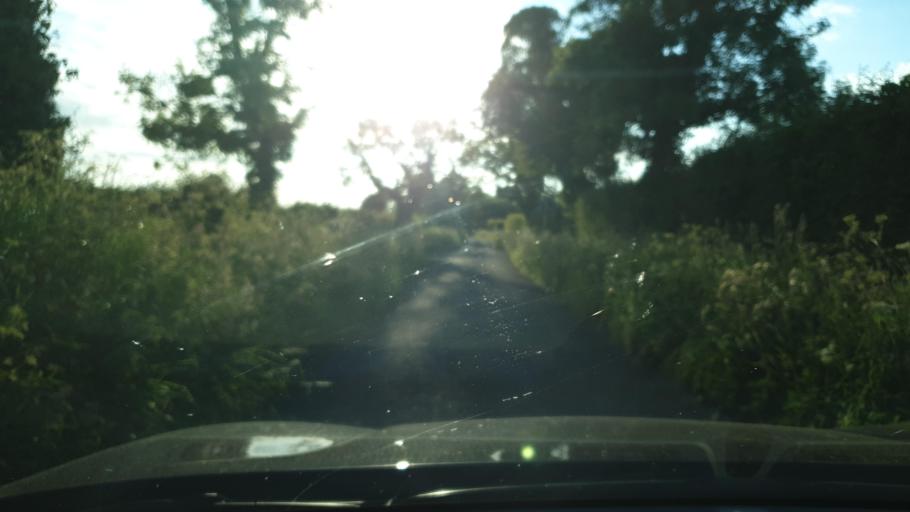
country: IE
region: Leinster
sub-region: An Mhi
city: Ratoath
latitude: 53.4868
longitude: -6.4344
